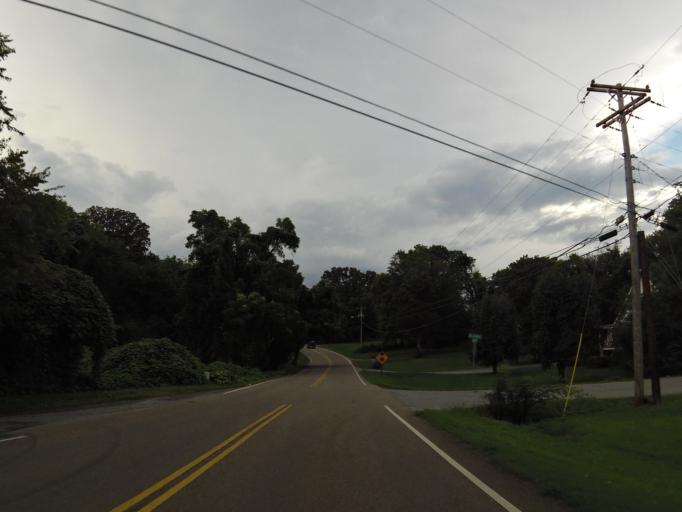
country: US
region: Tennessee
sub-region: Blount County
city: Alcoa
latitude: 35.7750
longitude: -84.0237
